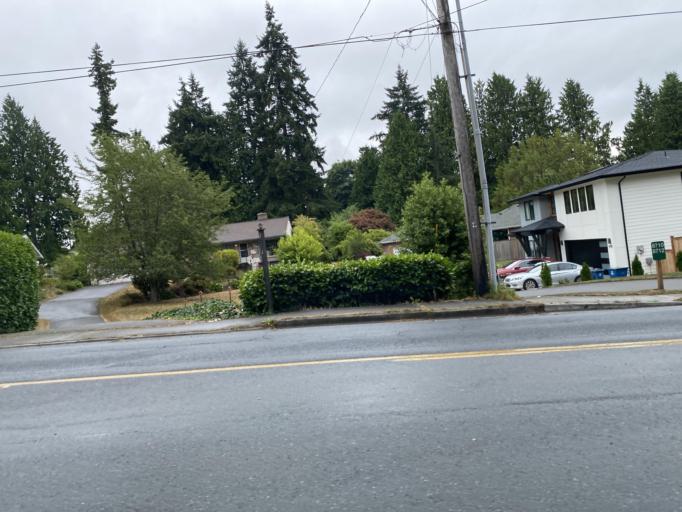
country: US
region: Washington
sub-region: Snohomish County
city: Edmonds
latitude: 47.8215
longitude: -122.3510
